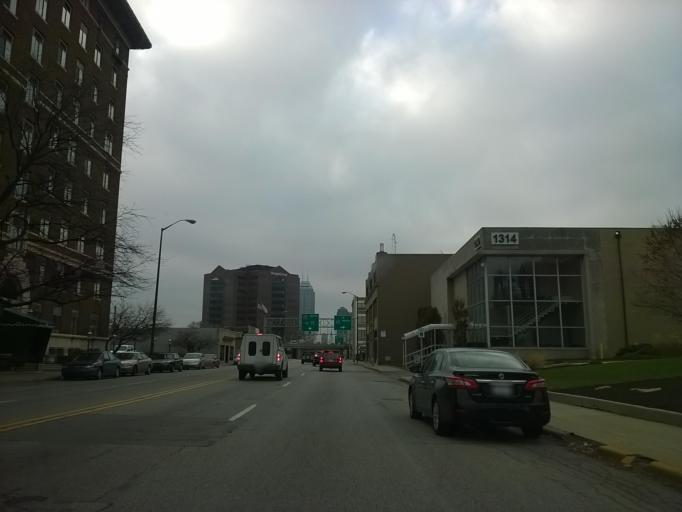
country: US
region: Indiana
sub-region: Marion County
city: Indianapolis
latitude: 39.7852
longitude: -86.1574
